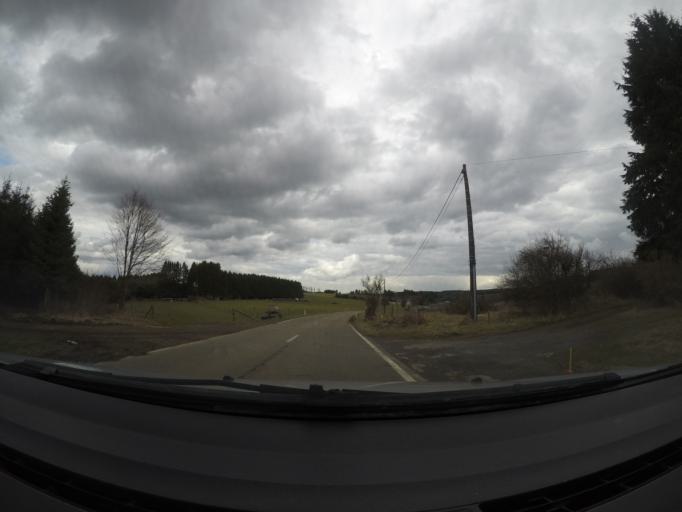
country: BE
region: Wallonia
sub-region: Province du Luxembourg
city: Leglise
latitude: 49.7651
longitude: 5.5035
